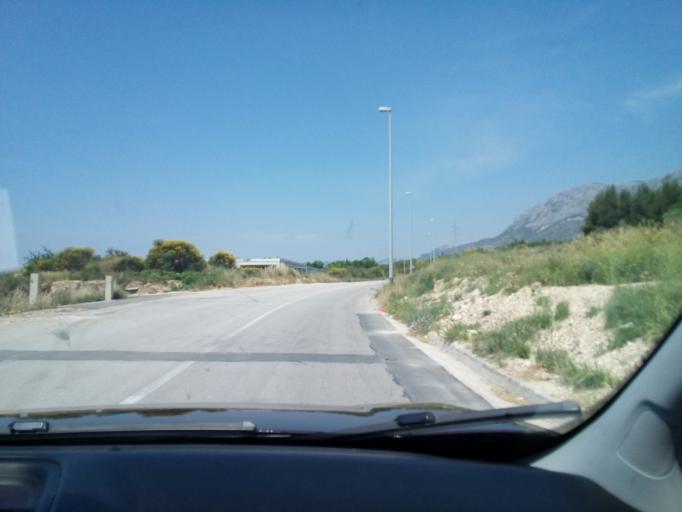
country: HR
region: Splitsko-Dalmatinska
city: Vranjic
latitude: 43.5458
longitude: 16.4558
